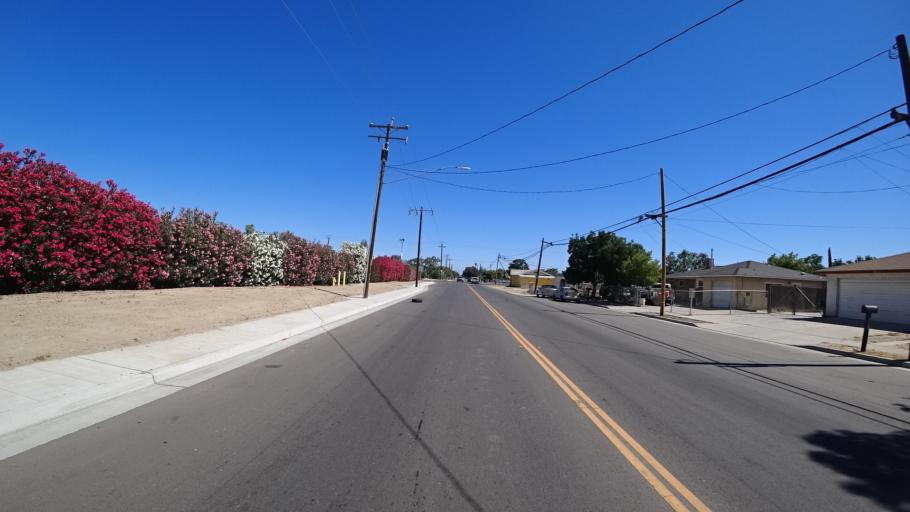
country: US
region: California
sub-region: Fresno County
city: Easton
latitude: 36.6913
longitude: -119.7999
